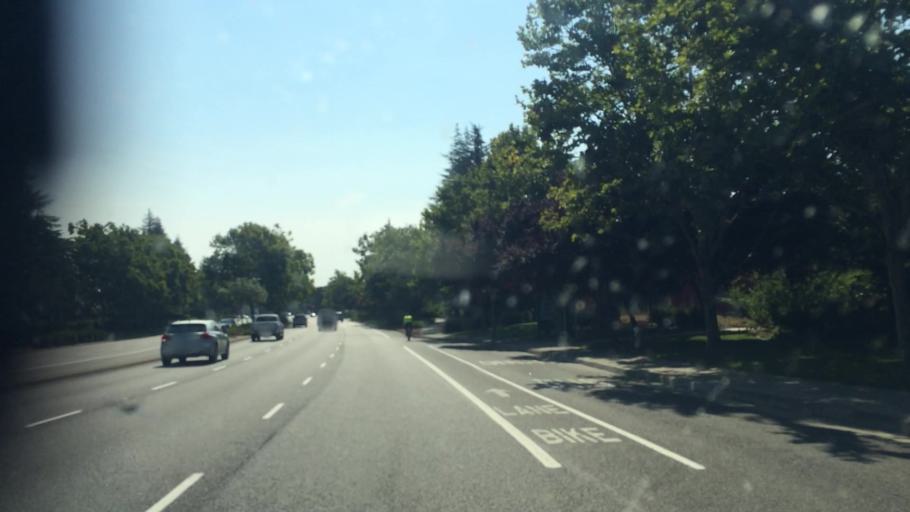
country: US
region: California
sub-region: Sacramento County
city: Laguna
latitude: 38.4232
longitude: -121.4526
